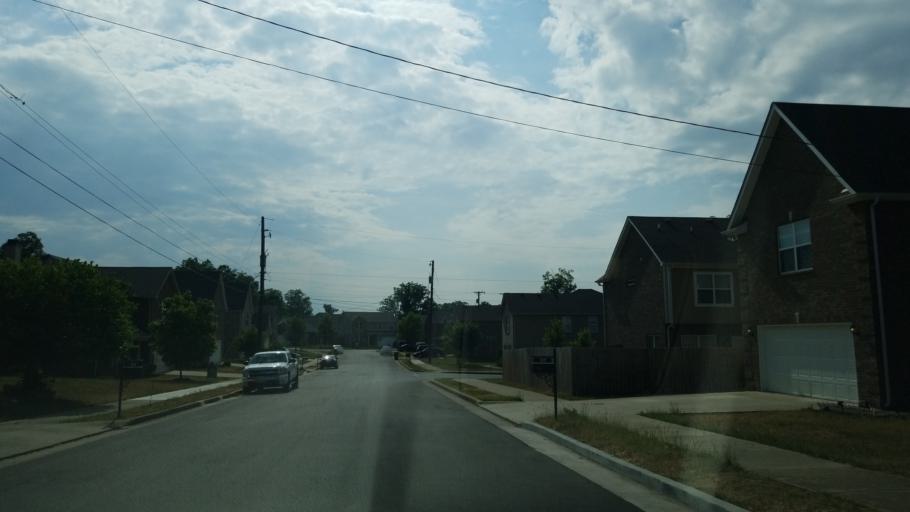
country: US
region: Tennessee
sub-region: Rutherford County
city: La Vergne
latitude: 36.0526
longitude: -86.5864
